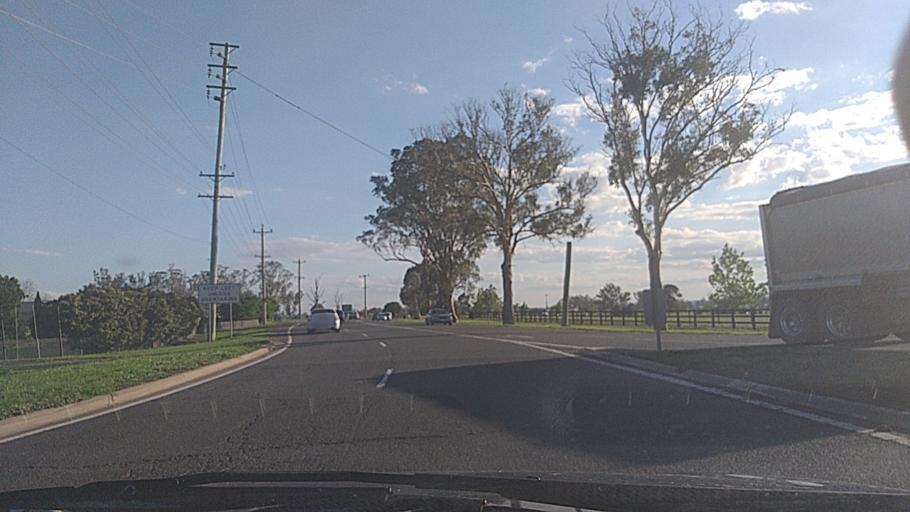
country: AU
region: New South Wales
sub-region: Liverpool
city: Luddenham
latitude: -33.8644
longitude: 150.6981
